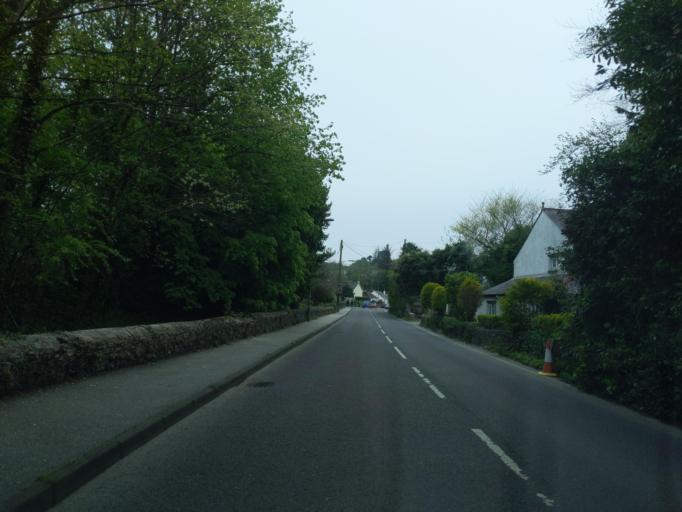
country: GB
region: England
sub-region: Cornwall
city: Par
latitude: 50.3532
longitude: -4.7107
